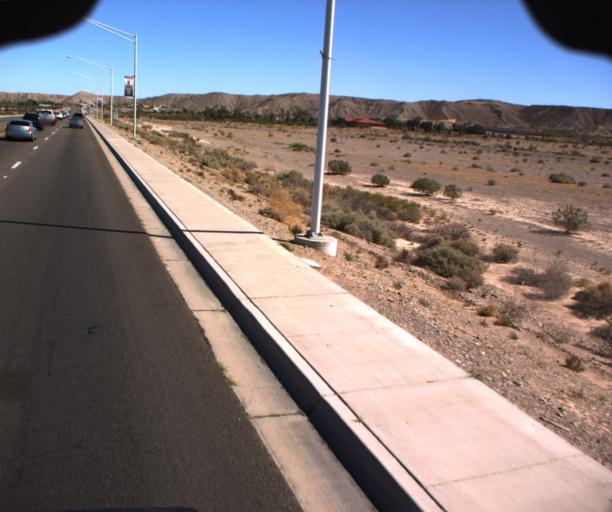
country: US
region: Arizona
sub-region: Mohave County
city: Bullhead City
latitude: 35.0576
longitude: -114.5891
